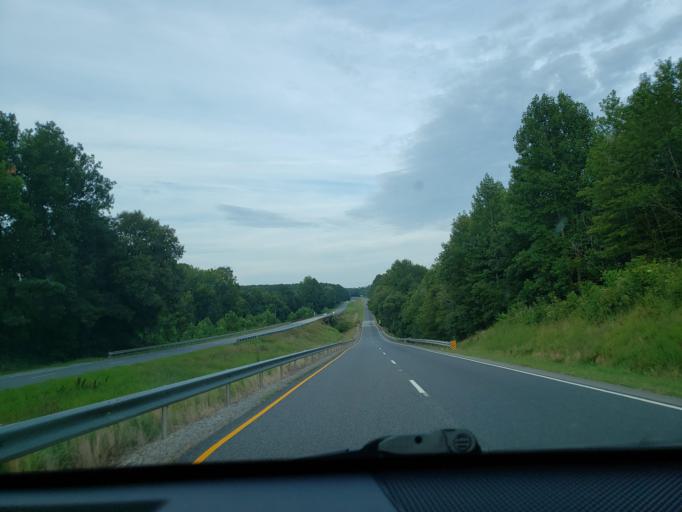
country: US
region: Virginia
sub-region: Brunswick County
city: Lawrenceville
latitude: 36.7235
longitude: -77.9368
